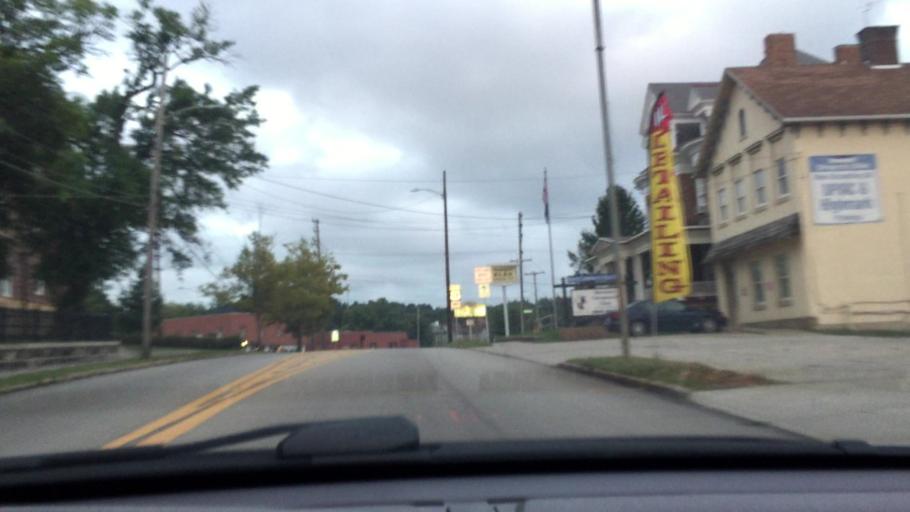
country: US
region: Pennsylvania
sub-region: Washington County
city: East Washington
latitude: 40.1683
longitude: -80.2415
